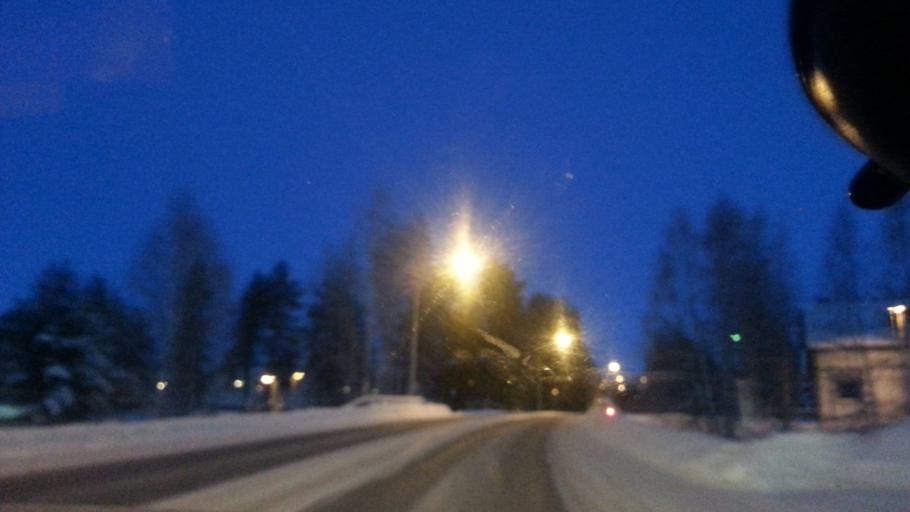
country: FI
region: Lapland
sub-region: Rovaniemi
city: Rovaniemi
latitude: 66.4943
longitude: 25.7567
